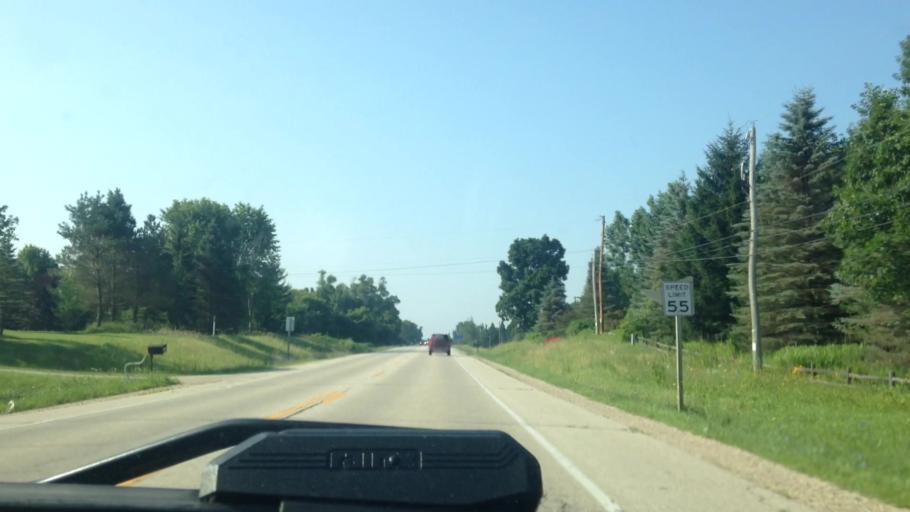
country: US
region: Wisconsin
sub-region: Washington County
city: Slinger
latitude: 43.2934
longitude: -88.2609
